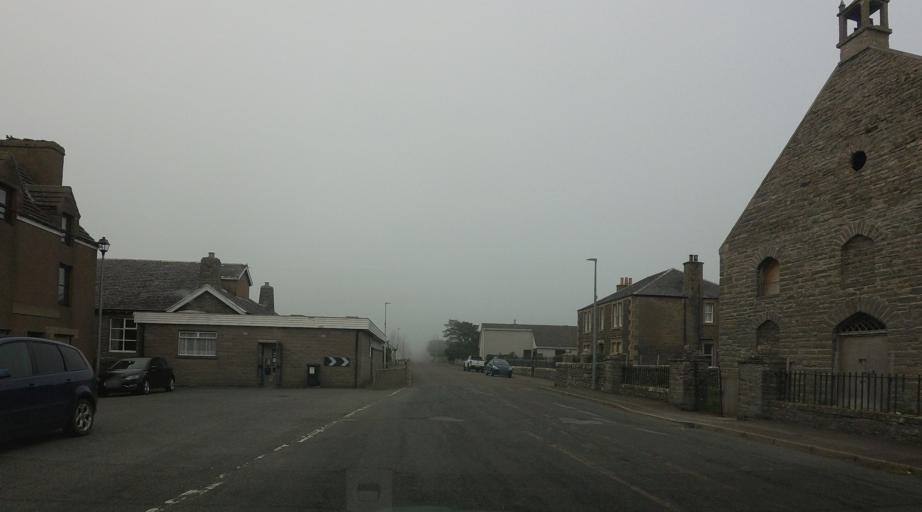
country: GB
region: Scotland
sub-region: Highland
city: Wick
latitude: 58.3027
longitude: -3.2850
